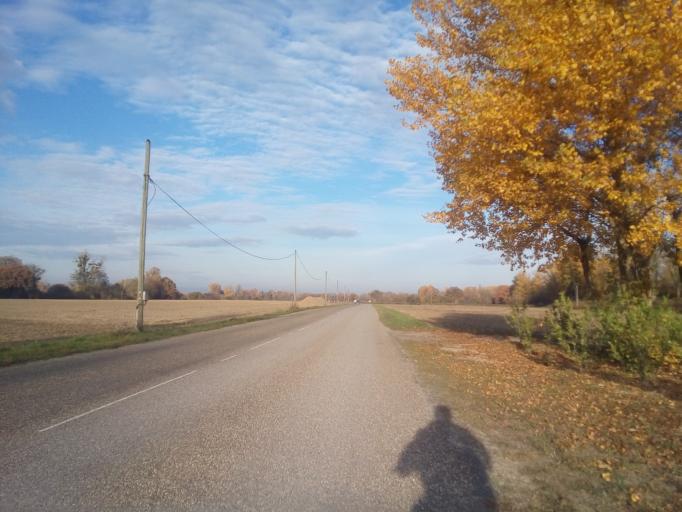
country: FR
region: Alsace
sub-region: Departement du Bas-Rhin
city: Gambsheim
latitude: 48.6945
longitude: 7.9165
